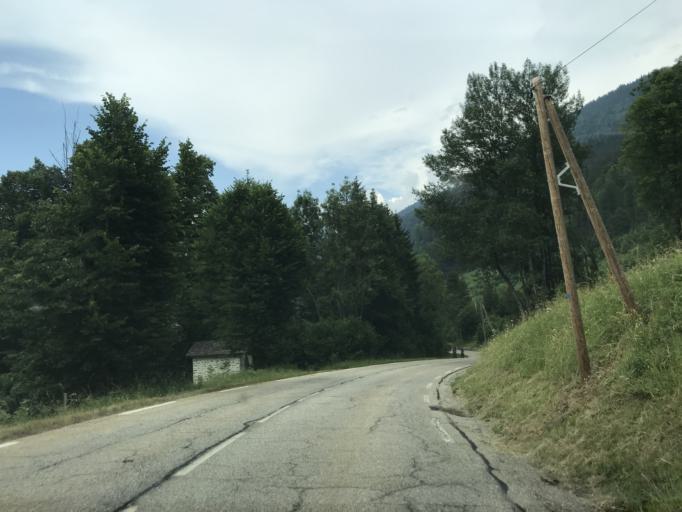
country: FR
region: Rhone-Alpes
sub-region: Departement de l'Isere
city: Allevard
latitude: 45.3233
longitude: 6.0877
